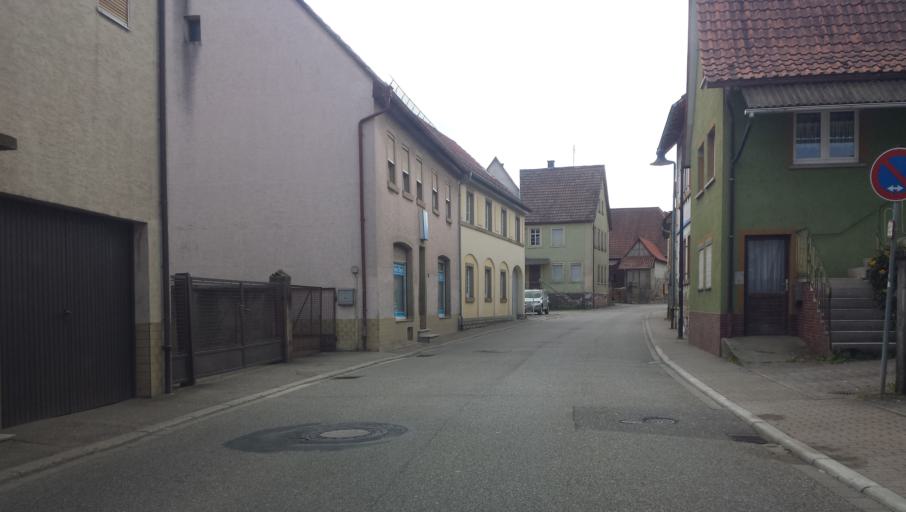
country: DE
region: Baden-Wuerttemberg
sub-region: Karlsruhe Region
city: Sinsheim
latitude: 49.2099
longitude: 8.8759
